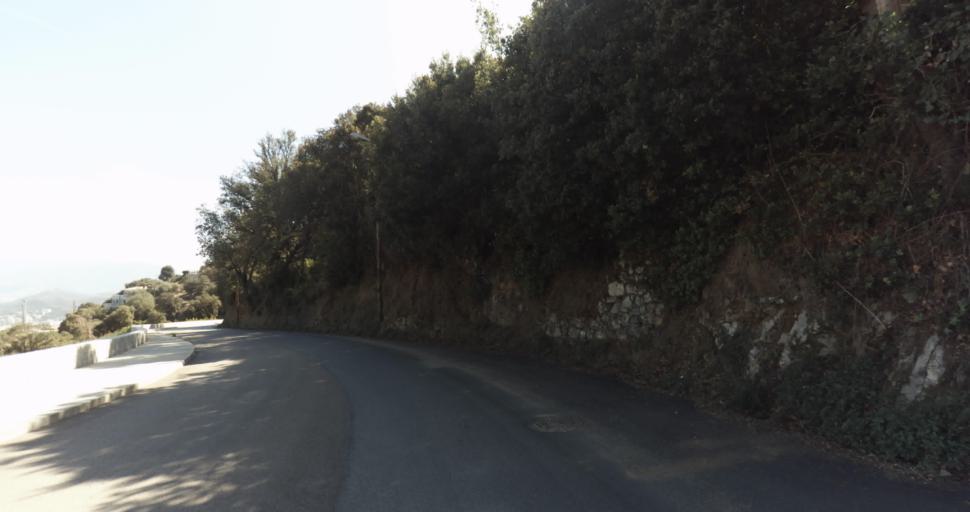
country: FR
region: Corsica
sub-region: Departement de la Corse-du-Sud
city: Ajaccio
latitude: 41.9243
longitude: 8.7198
